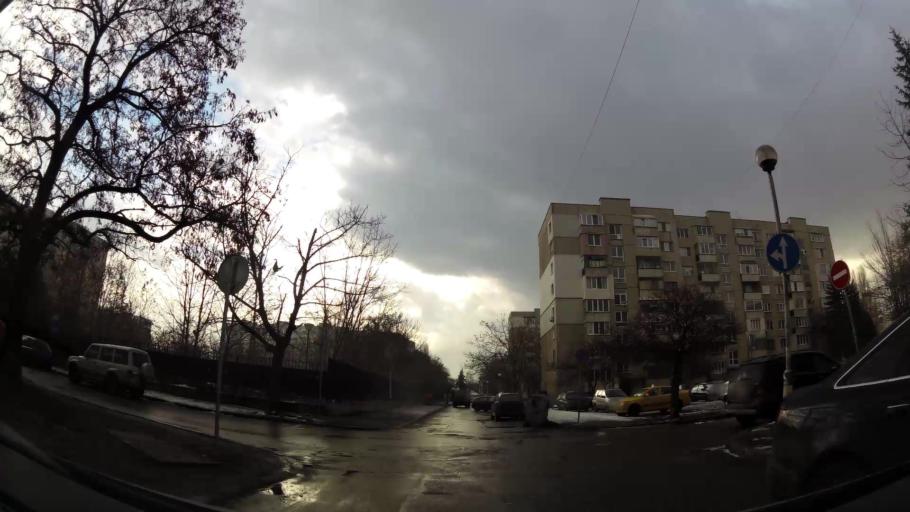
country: BG
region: Sofia-Capital
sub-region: Stolichna Obshtina
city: Sofia
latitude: 42.6993
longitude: 23.2879
